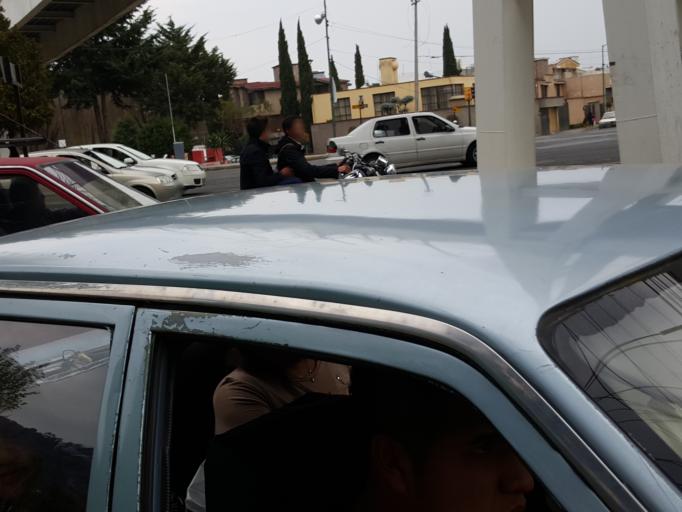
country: MX
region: Mexico
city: San Buenaventura
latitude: 19.2849
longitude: -99.6749
